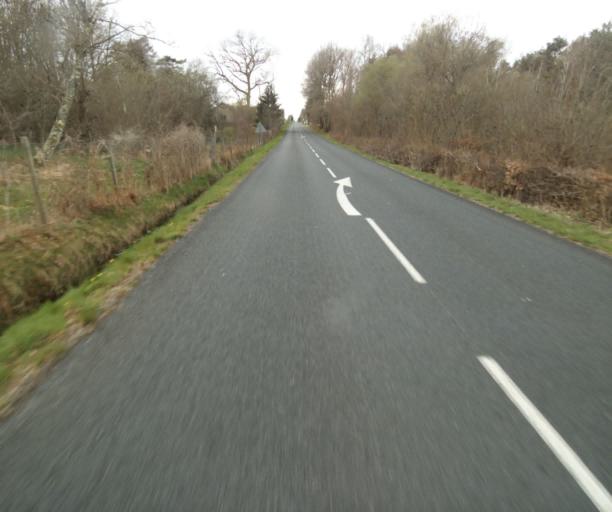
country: FR
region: Limousin
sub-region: Departement de la Correze
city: Egletons
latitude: 45.2774
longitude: 1.9828
